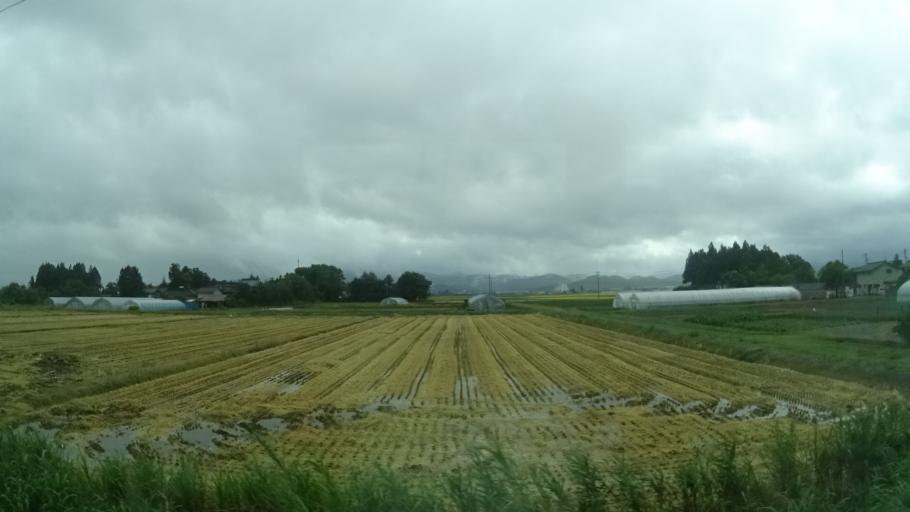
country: JP
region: Yamagata
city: Tsuruoka
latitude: 38.7427
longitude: 139.7825
